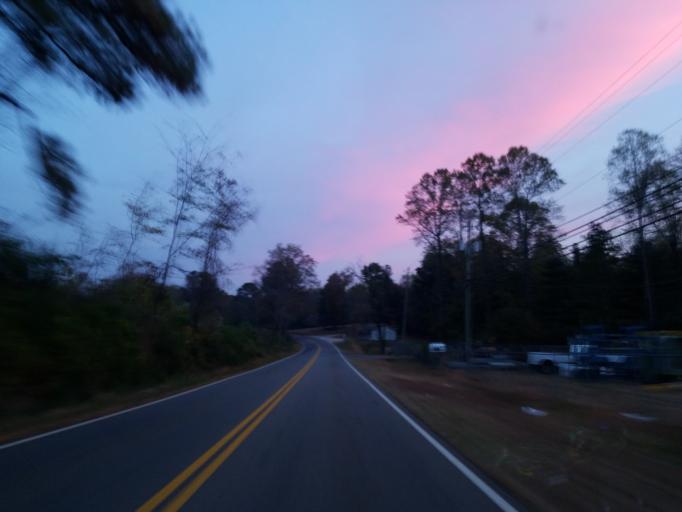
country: US
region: Georgia
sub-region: Pickens County
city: Jasper
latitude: 34.4845
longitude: -84.4562
